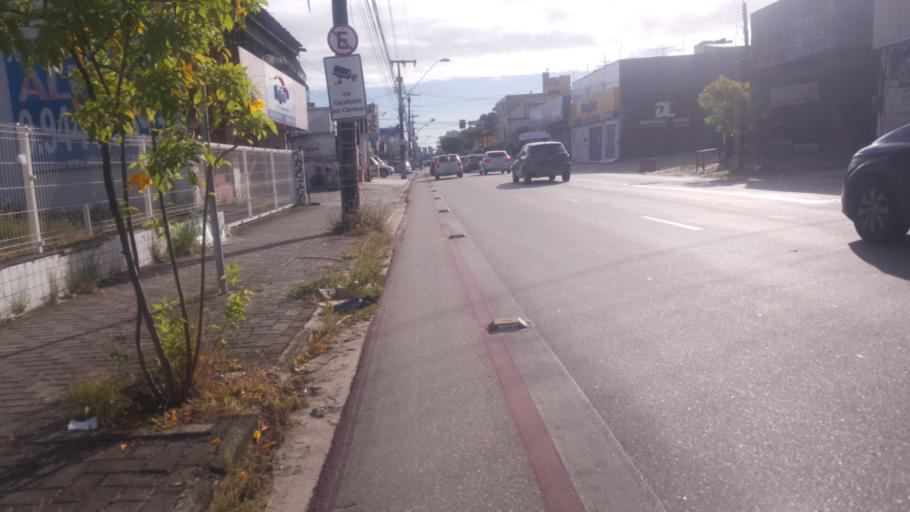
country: BR
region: Ceara
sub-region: Fortaleza
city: Fortaleza
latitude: -3.7672
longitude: -38.5508
